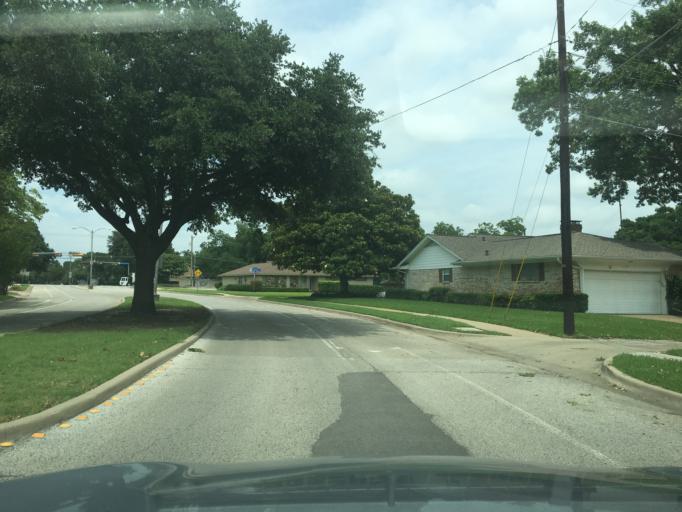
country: US
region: Texas
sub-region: Dallas County
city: Richardson
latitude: 32.9499
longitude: -96.7561
